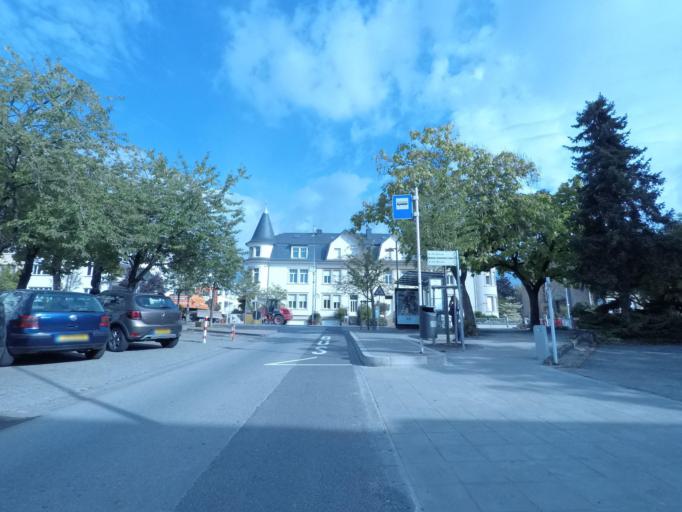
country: LU
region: Luxembourg
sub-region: Canton de Luxembourg
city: Luxembourg
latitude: 49.6033
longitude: 6.1185
